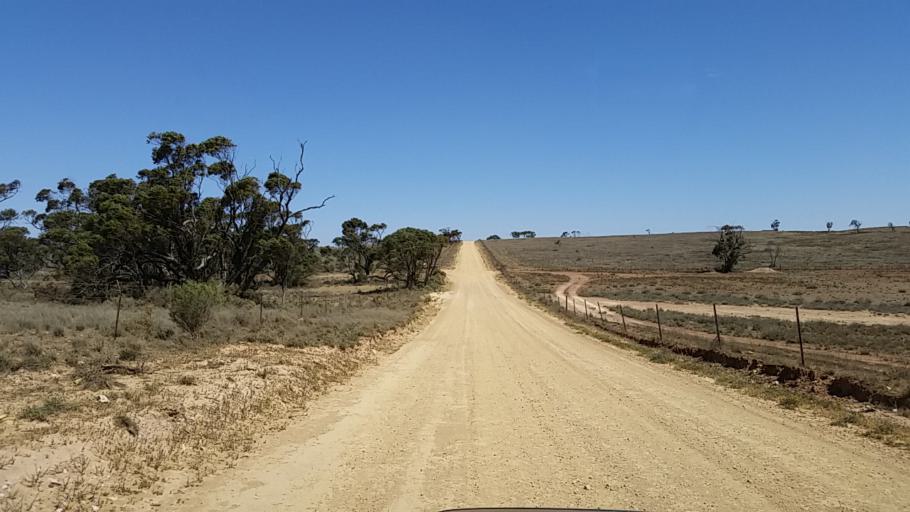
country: AU
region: South Australia
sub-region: Peterborough
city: Peterborough
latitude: -32.9832
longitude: 138.8318
